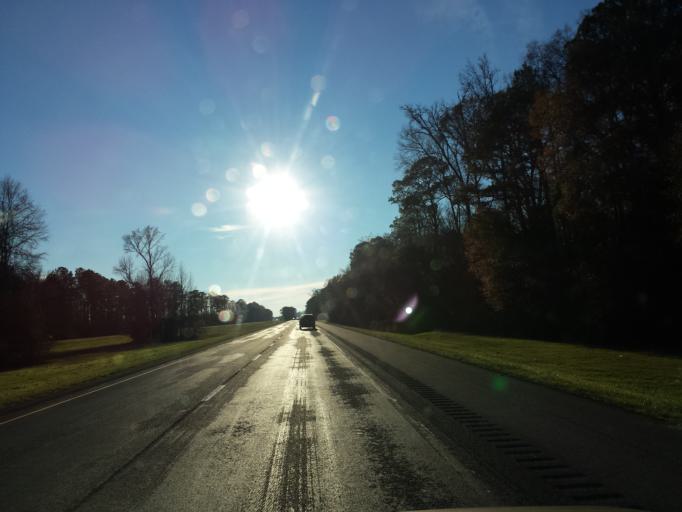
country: US
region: Alabama
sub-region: Greene County
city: Eutaw
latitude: 32.8183
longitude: -87.9986
